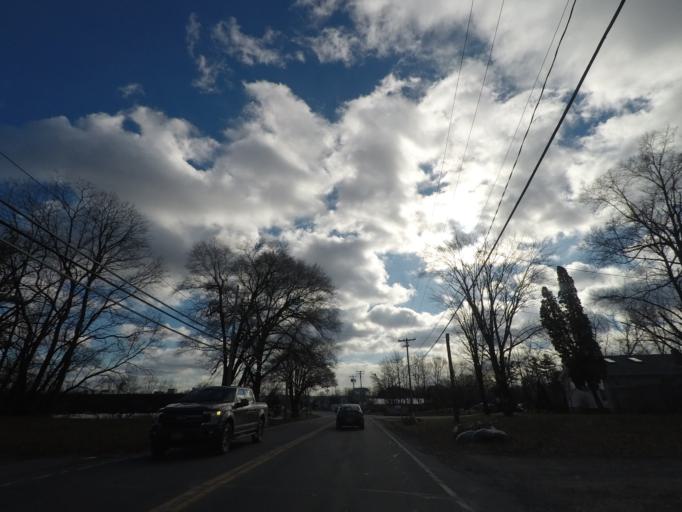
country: US
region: New York
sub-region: Schenectady County
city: Scotia
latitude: 42.8452
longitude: -73.9418
